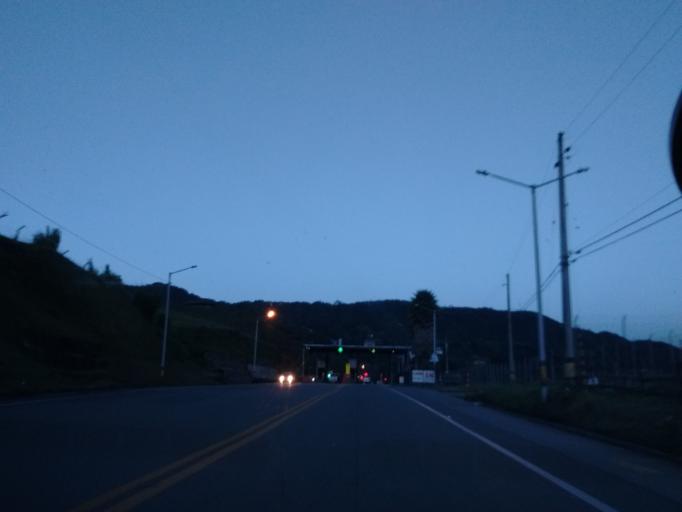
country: CO
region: Antioquia
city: Santuario
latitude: 6.1247
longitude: -75.2440
